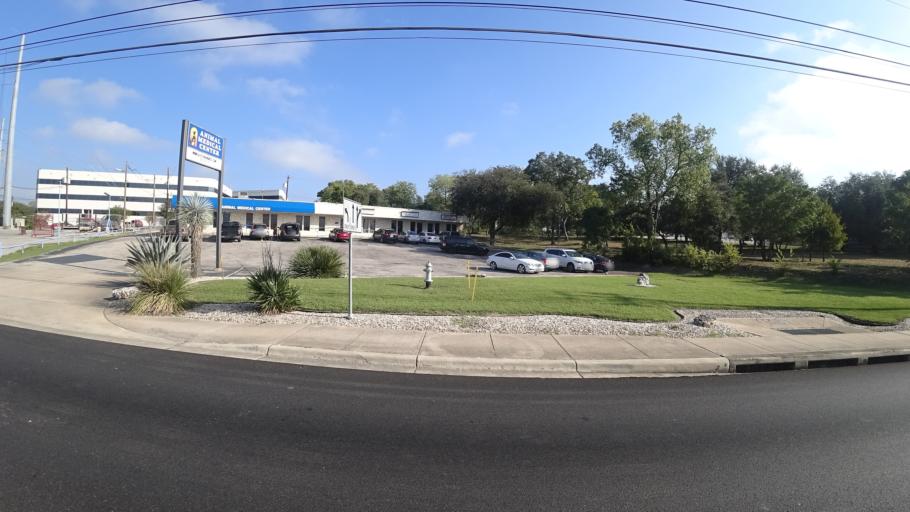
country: US
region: Texas
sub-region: Travis County
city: Austin
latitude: 30.3321
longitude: -97.6846
